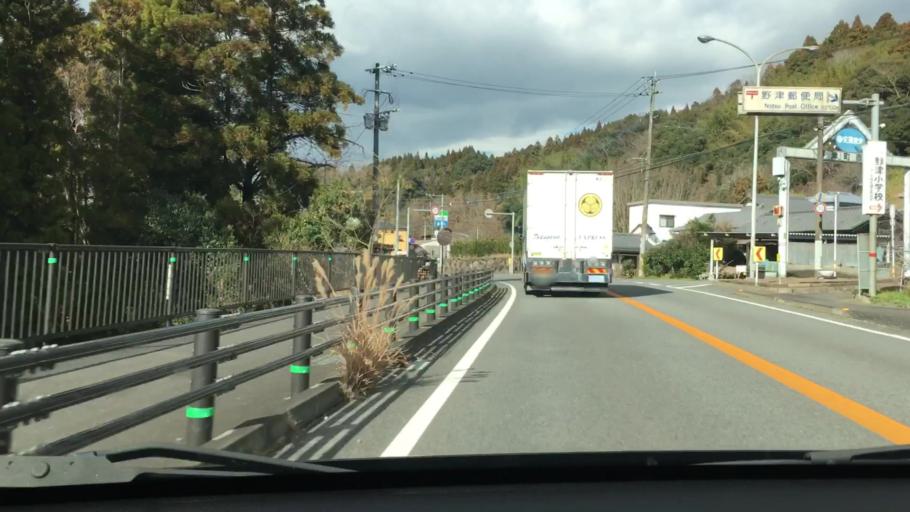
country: JP
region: Oita
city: Usuki
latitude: 33.0462
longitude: 131.6918
